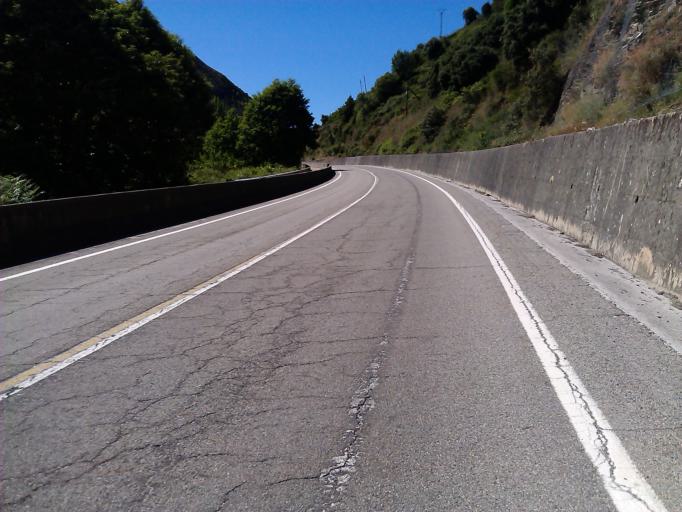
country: ES
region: Castille and Leon
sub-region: Provincia de Leon
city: Villafranca del Bierzo
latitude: 42.6168
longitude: -6.8261
